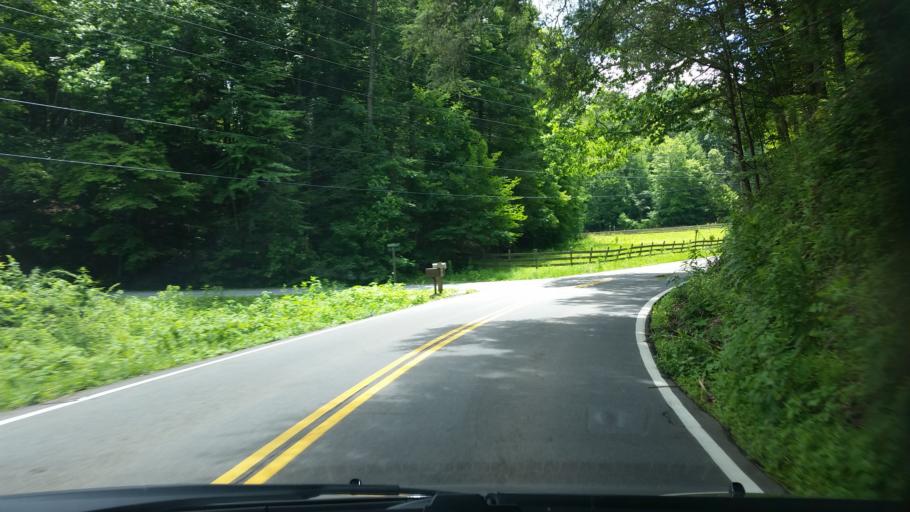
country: US
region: Tennessee
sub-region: Sevier County
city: Gatlinburg
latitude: 35.7475
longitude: -83.4321
